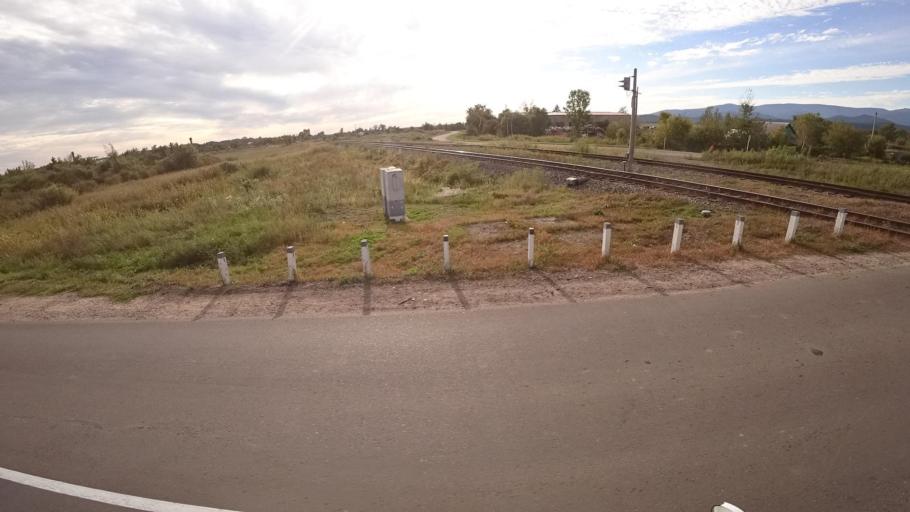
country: RU
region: Primorskiy
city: Dostoyevka
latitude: 44.2966
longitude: 133.4265
